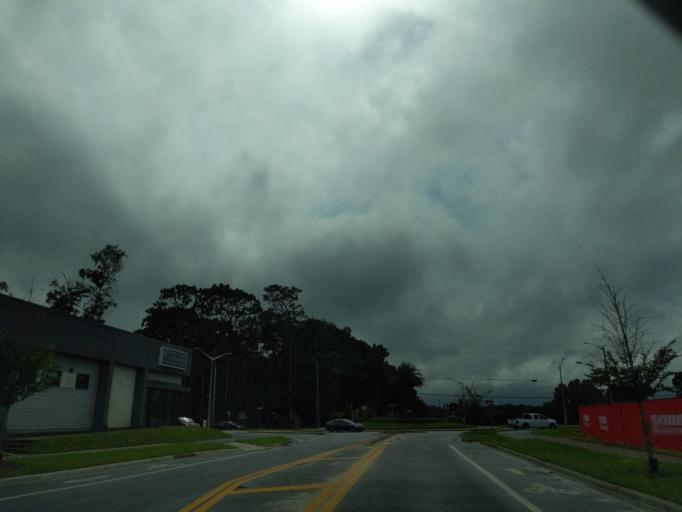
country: US
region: Florida
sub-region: Alachua County
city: Gainesville
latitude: 29.6380
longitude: -82.4216
